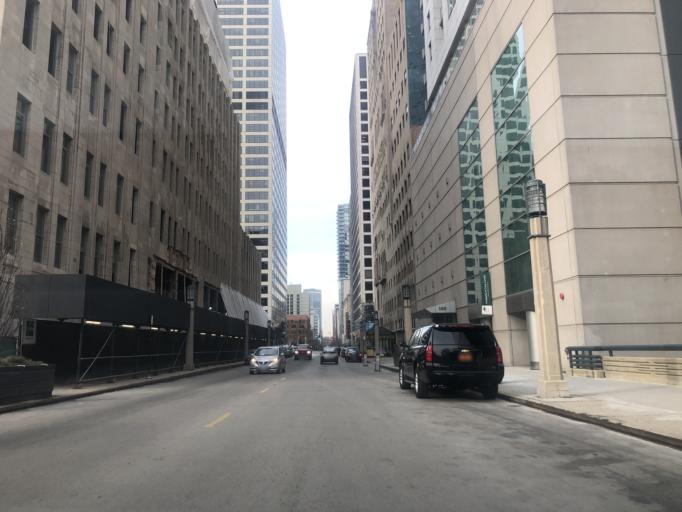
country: US
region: Illinois
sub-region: Cook County
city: Chicago
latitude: 41.8909
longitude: -87.6225
